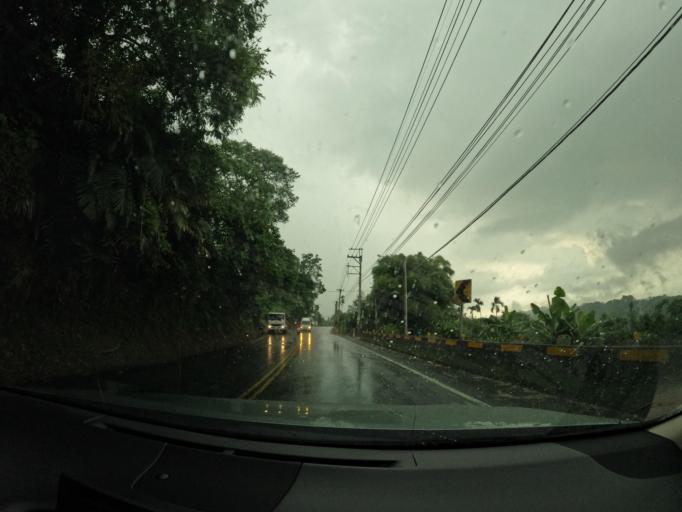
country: TW
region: Taiwan
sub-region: Nantou
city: Nantou
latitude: 23.8863
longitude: 120.7523
